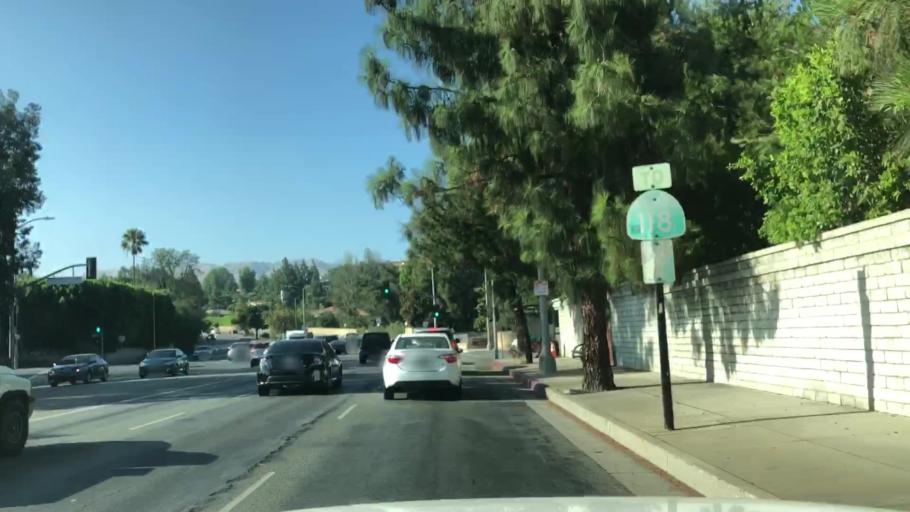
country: US
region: California
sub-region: Los Angeles County
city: Northridge
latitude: 34.2567
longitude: -118.5536
